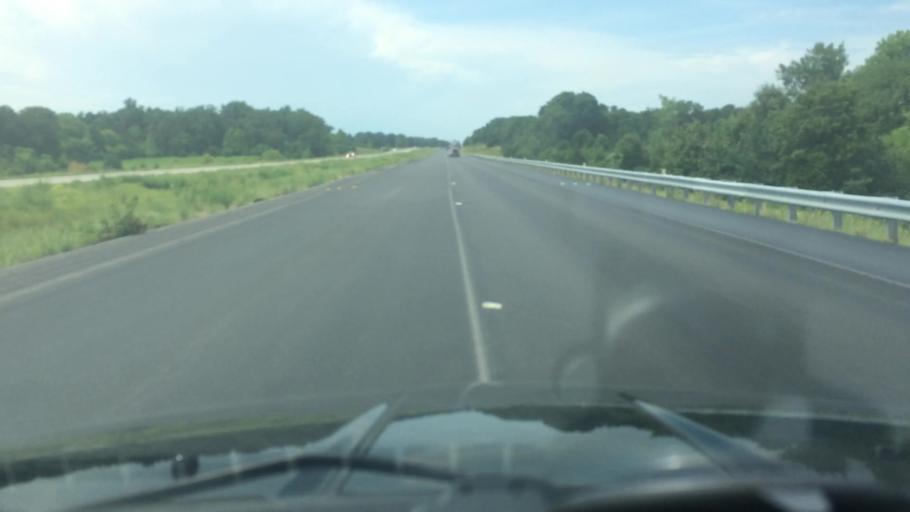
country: US
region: Missouri
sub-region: Saint Clair County
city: Osceola
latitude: 37.9451
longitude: -93.6360
